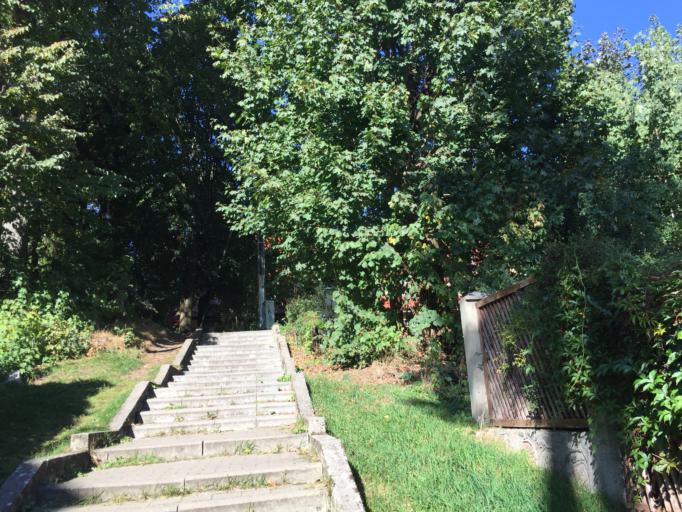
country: RU
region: Kaliningrad
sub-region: Gorod Svetlogorsk
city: Svetlogorsk
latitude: 54.9423
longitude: 20.1464
